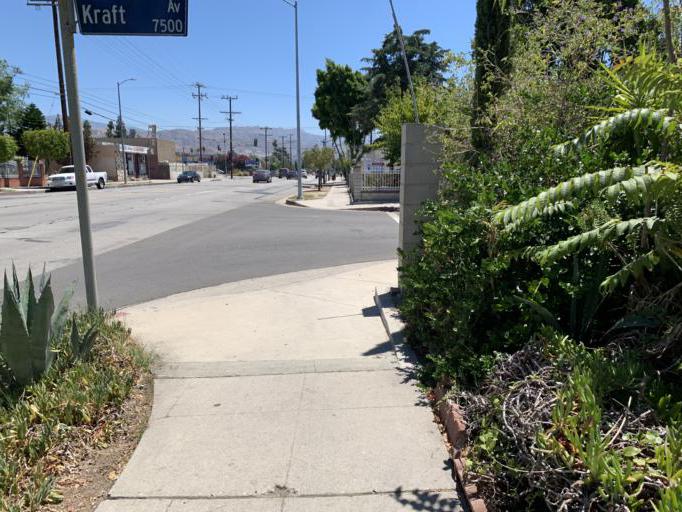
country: US
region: California
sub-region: Los Angeles County
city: North Hollywood
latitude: 34.2084
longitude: -118.3804
